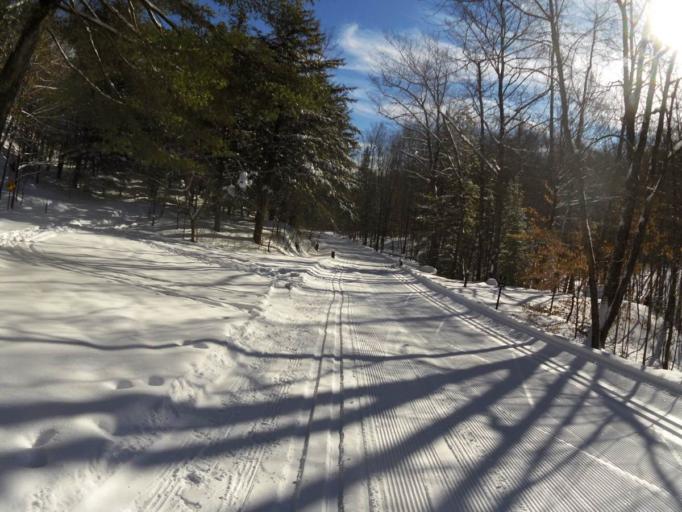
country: CA
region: Quebec
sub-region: Outaouais
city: Wakefield
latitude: 45.6003
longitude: -76.0063
